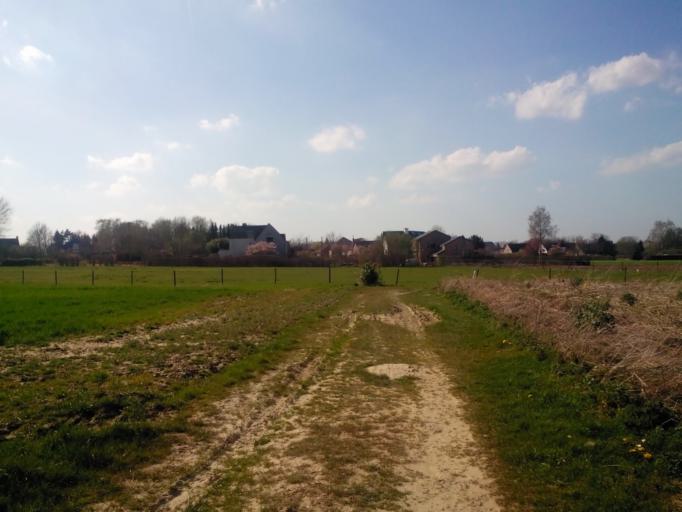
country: BE
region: Flanders
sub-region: Provincie Vlaams-Brabant
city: Bierbeek
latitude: 50.8355
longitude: 4.7164
